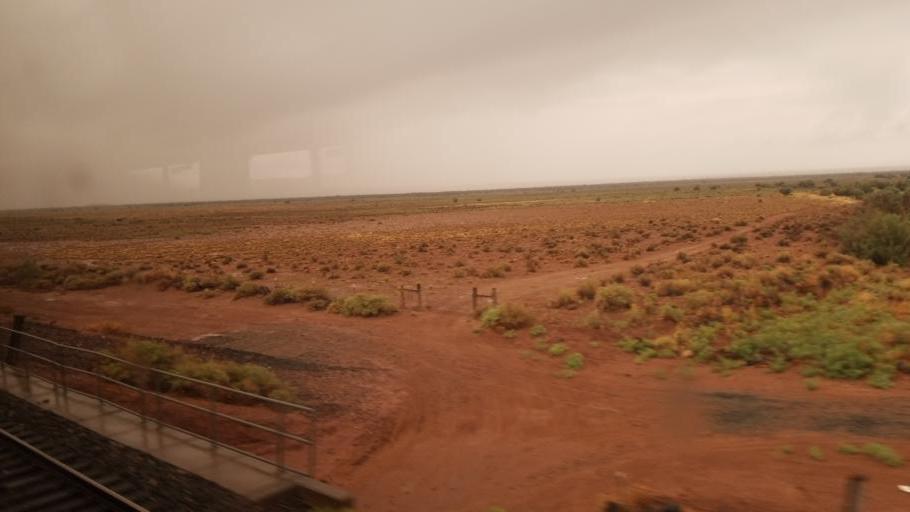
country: US
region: Arizona
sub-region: Navajo County
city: Joseph City
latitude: 34.9676
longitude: -110.5047
